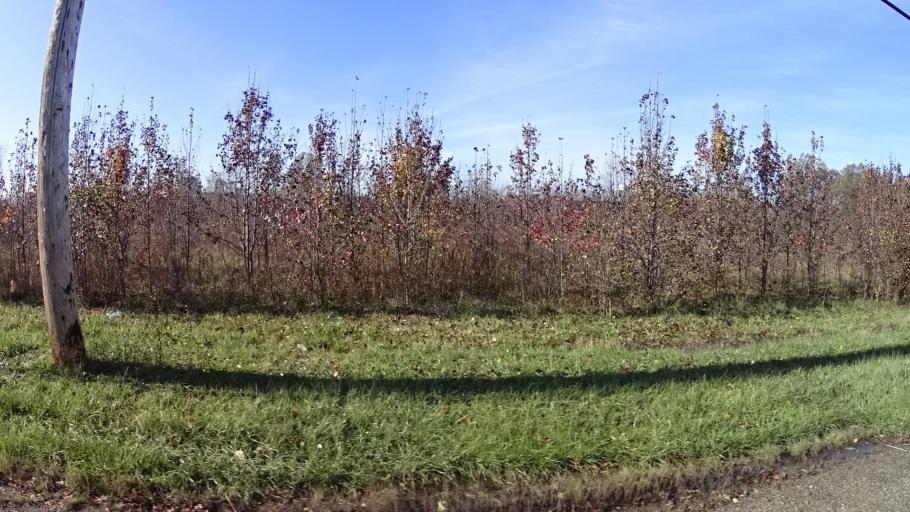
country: US
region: Ohio
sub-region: Lorain County
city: Avon Lake
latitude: 41.4916
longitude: -82.0470
